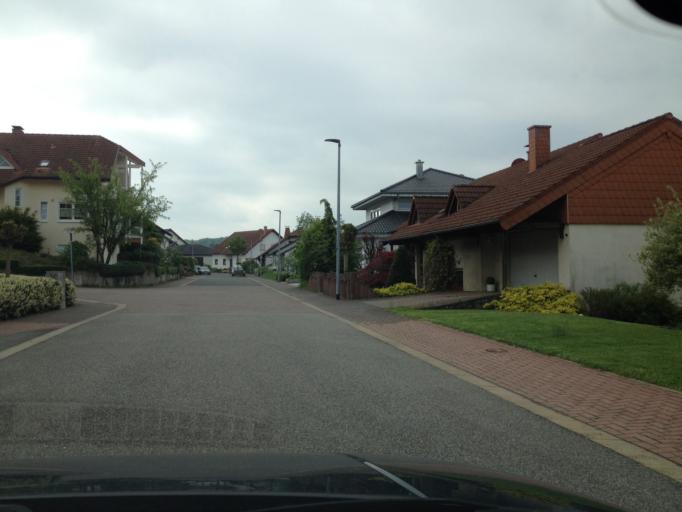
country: DE
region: Saarland
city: Hangard
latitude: 49.3976
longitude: 7.2462
